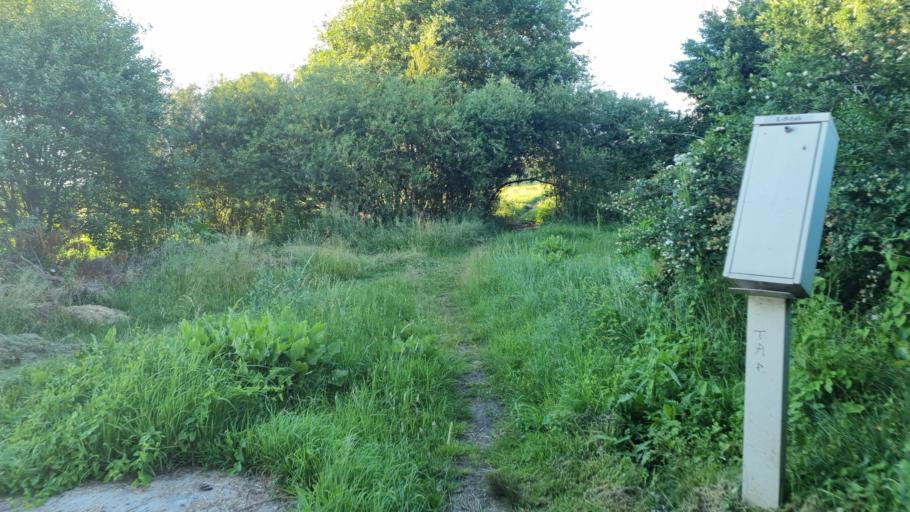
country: LV
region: Kekava
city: Balozi
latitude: 56.8913
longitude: 24.1634
